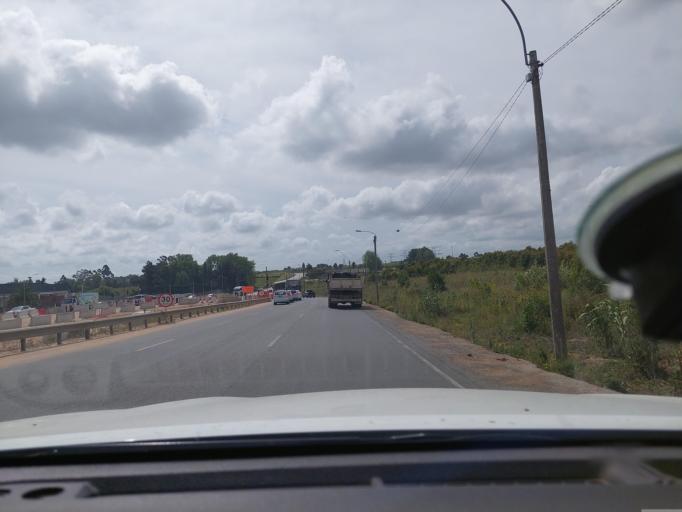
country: UY
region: Canelones
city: La Paz
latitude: -34.7827
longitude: -56.2262
